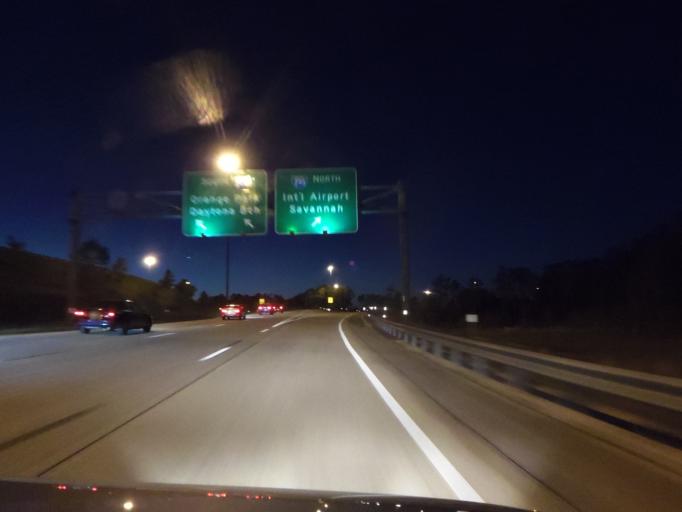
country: US
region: Florida
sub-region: Duval County
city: Jacksonville Beach
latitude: 30.2547
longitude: -81.5133
